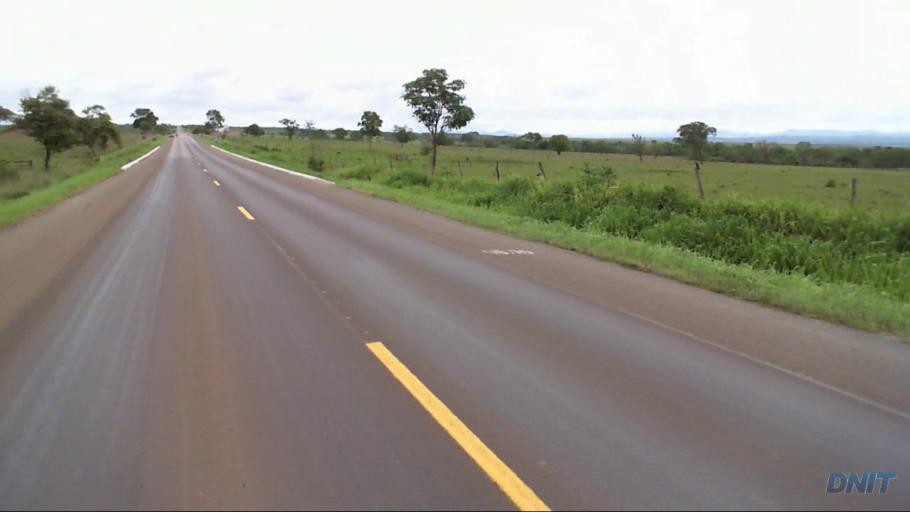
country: BR
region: Goias
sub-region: Padre Bernardo
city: Padre Bernardo
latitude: -15.1612
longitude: -48.3093
